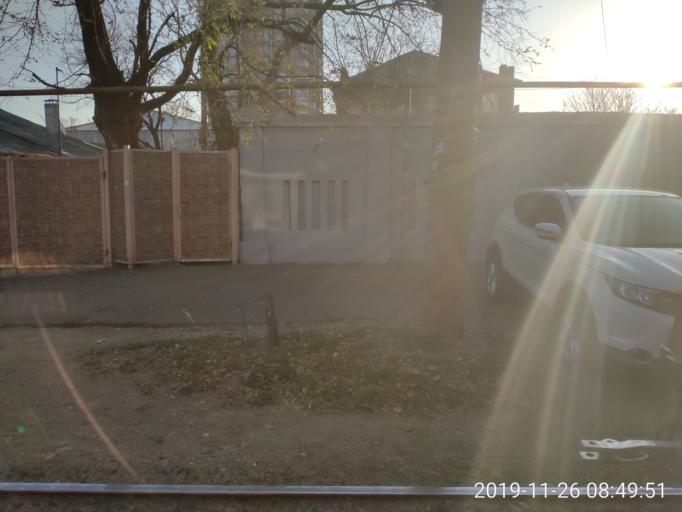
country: RU
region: Krasnodarskiy
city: Krasnodar
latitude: 45.0327
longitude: 38.9775
